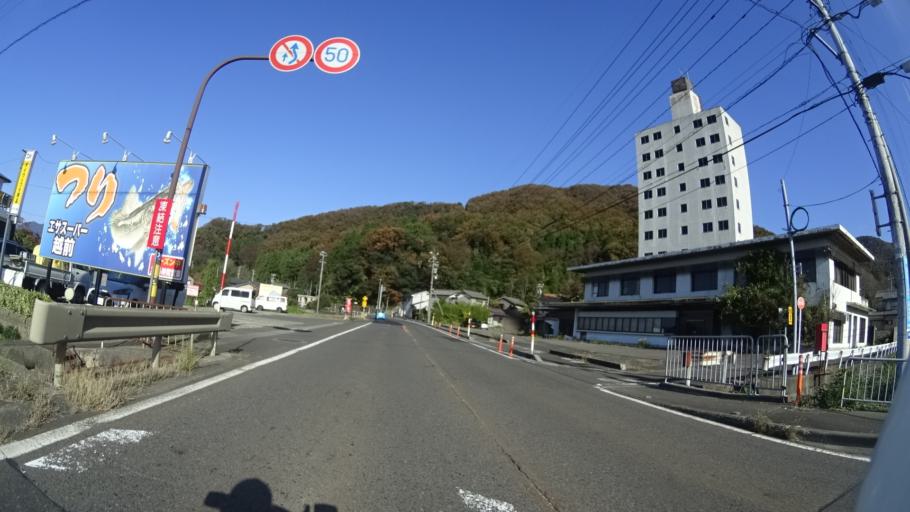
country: JP
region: Fukui
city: Tsuruga
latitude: 35.6870
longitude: 136.0864
